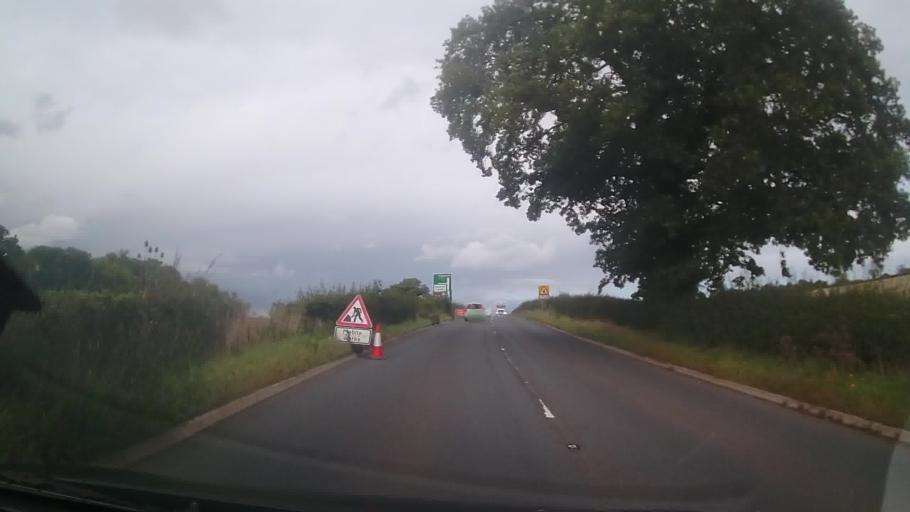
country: GB
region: England
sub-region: Shropshire
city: Alveley
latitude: 52.4775
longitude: -2.3539
